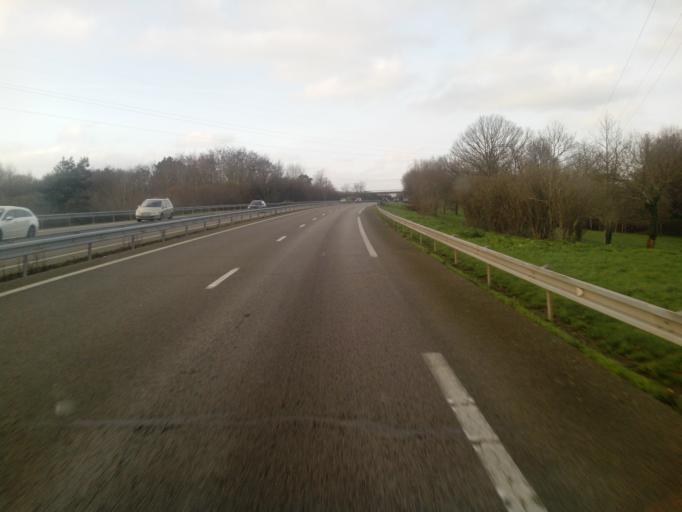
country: FR
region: Brittany
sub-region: Departement du Morbihan
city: Ploermel
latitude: 47.9232
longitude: -2.4121
